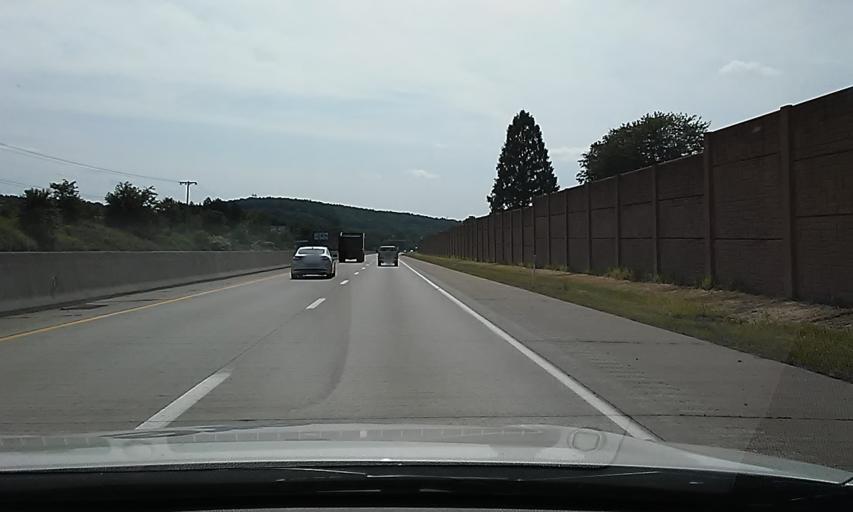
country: US
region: Pennsylvania
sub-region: Indiana County
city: Black Lick
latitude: 40.5031
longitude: -79.1692
